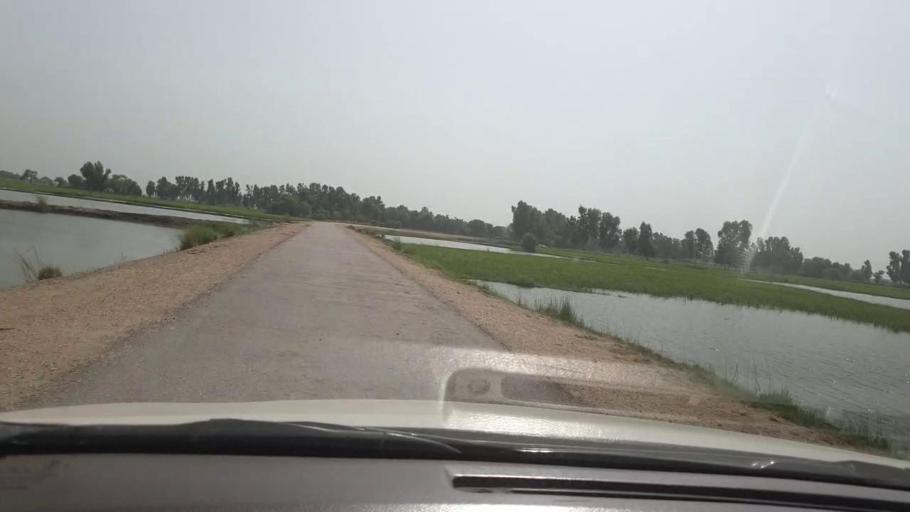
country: PK
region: Sindh
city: Rustam jo Goth
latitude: 27.9736
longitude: 68.7738
